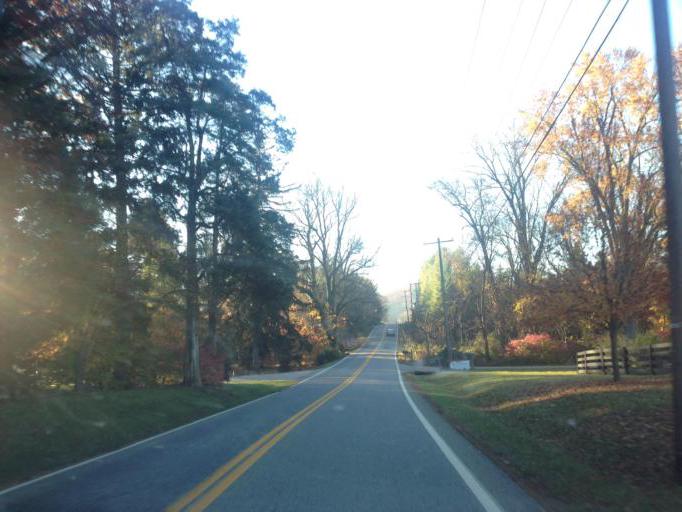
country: US
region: Maryland
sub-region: Baltimore County
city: Mays Chapel
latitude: 39.4204
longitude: -76.6902
